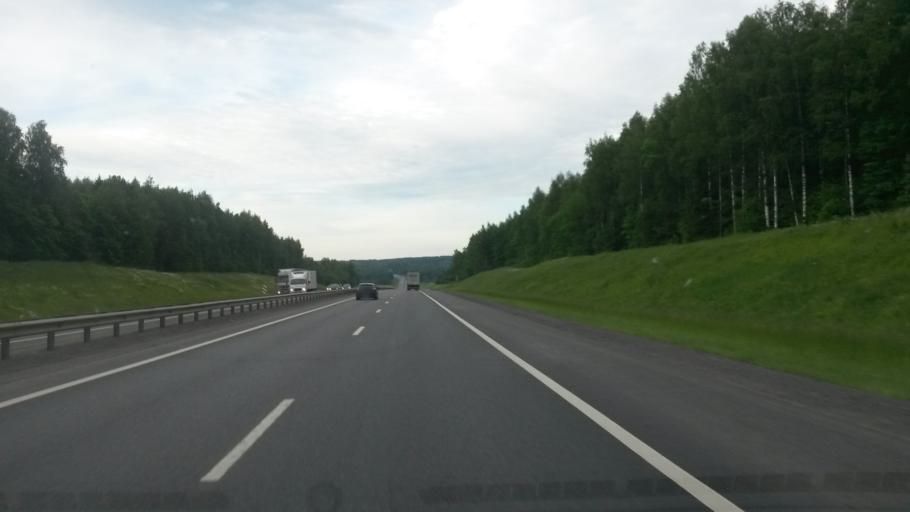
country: RU
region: Vladimir
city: Strunino
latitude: 56.5256
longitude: 38.5682
